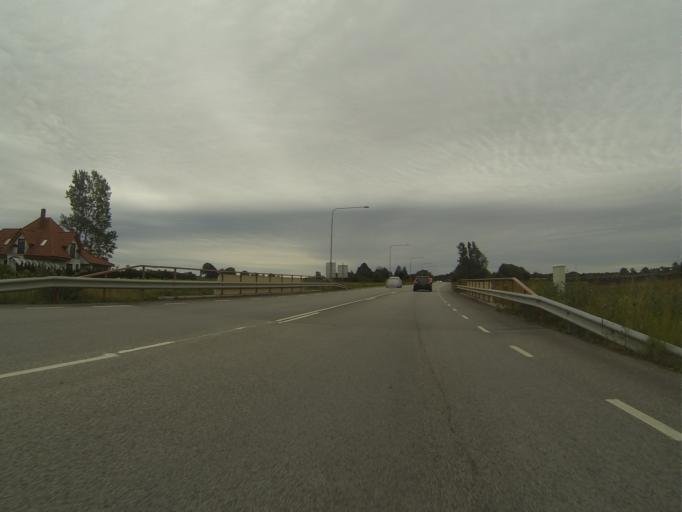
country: SE
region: Skane
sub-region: Burlovs Kommun
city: Arloev
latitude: 55.5940
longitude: 13.1013
